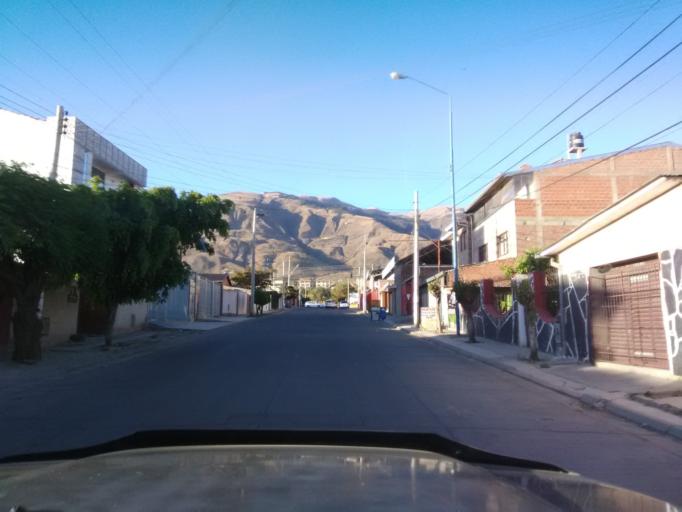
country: BO
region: Cochabamba
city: Cochabamba
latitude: -17.3563
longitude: -66.1816
